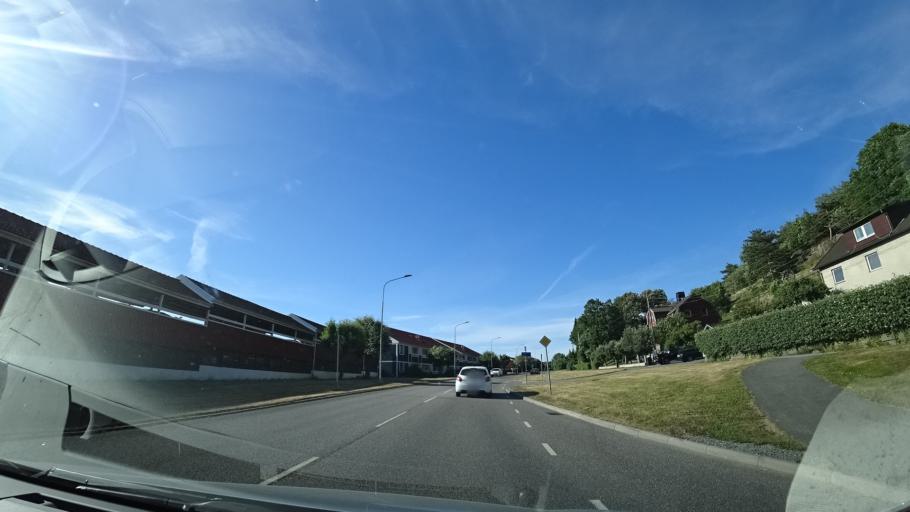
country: SE
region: Vaestra Goetaland
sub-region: Goteborg
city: Billdal
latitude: 57.5867
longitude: 11.9392
